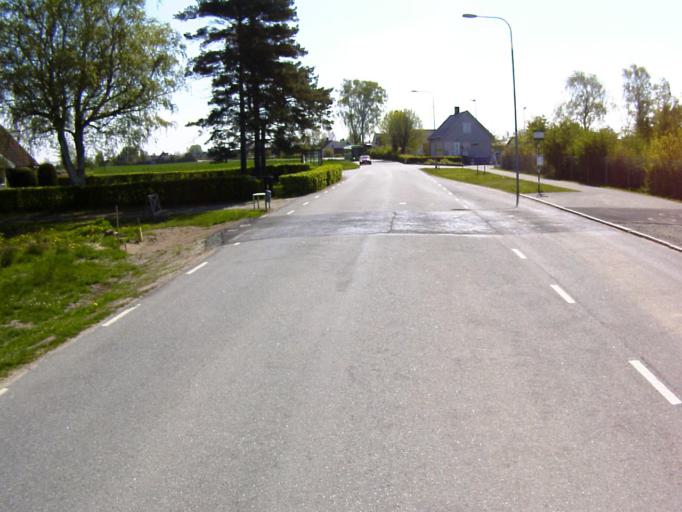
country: SE
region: Skane
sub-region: Kristianstads Kommun
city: Fjalkinge
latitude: 56.0187
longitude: 14.2239
